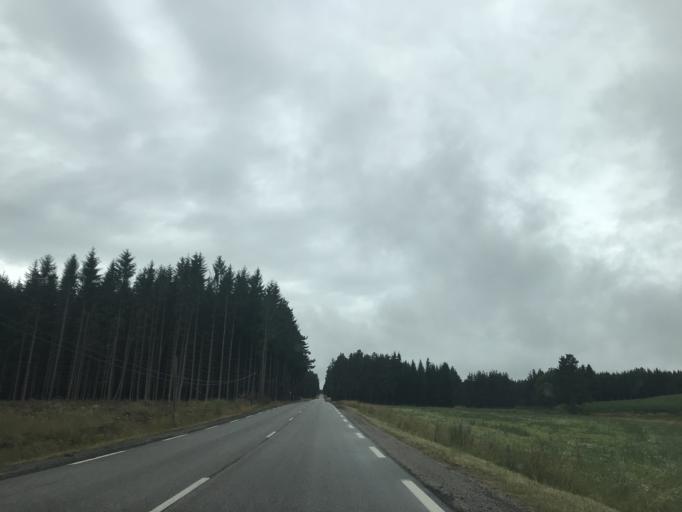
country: FR
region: Auvergne
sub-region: Departement de la Haute-Loire
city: Fontannes
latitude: 45.2343
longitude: 3.7944
